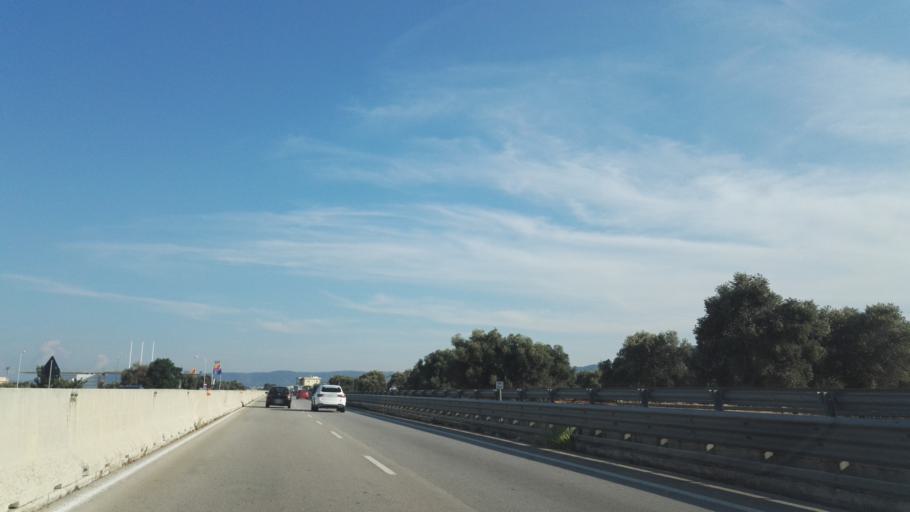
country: IT
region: Apulia
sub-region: Provincia di Brindisi
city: Fasano
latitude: 40.8652
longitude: 17.3461
